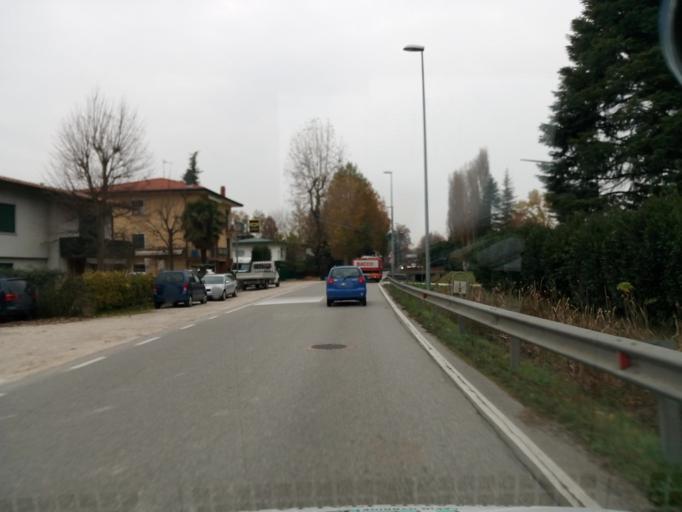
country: IT
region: Veneto
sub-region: Provincia di Padova
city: Vigonza
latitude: 45.4399
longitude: 11.9619
